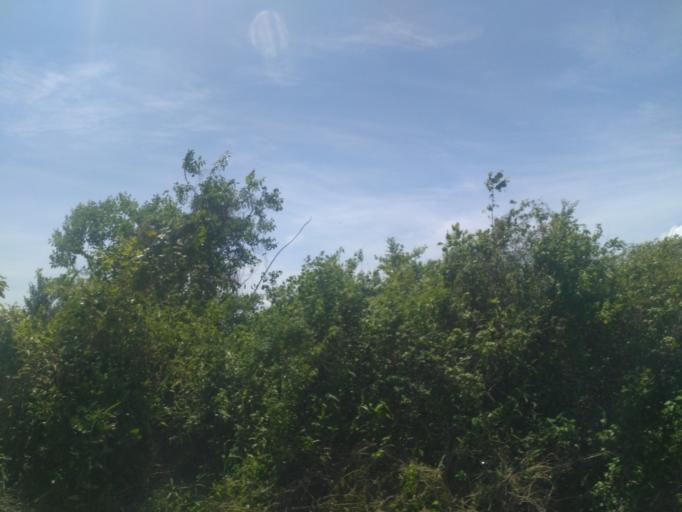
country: TZ
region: Zanzibar North
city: Gamba
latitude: -5.9259
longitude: 39.3497
